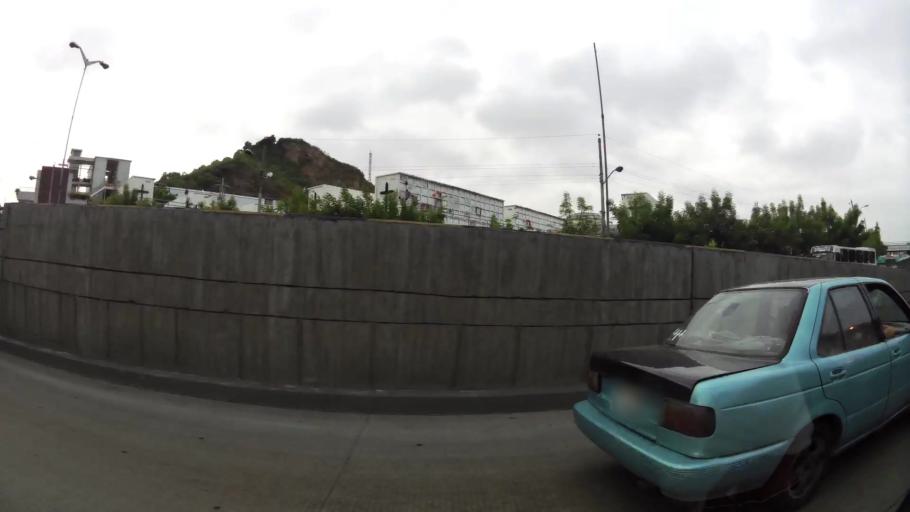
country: EC
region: Guayas
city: Guayaquil
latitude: -2.1820
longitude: -79.8894
